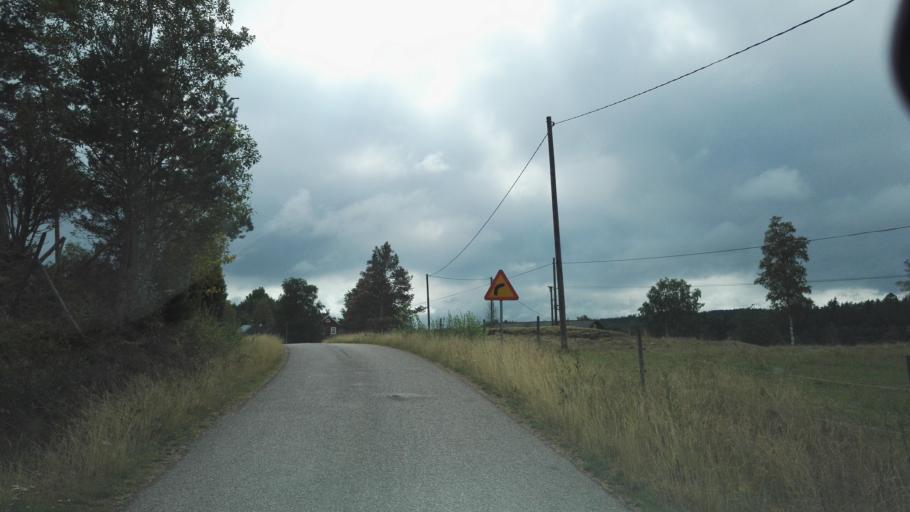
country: SE
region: Joenkoeping
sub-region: Vetlanda Kommun
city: Landsbro
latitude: 57.2209
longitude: 14.9660
